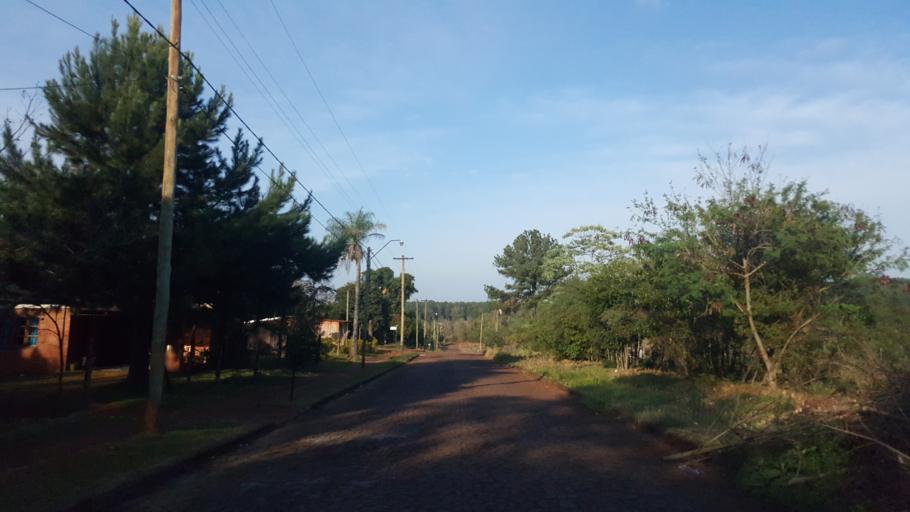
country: AR
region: Misiones
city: Capiovi
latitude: -26.8894
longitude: -55.0719
